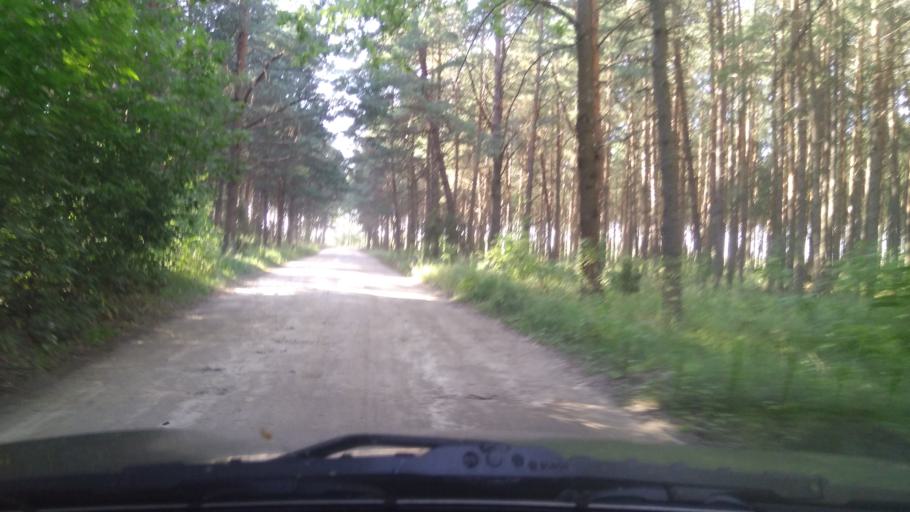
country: BY
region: Brest
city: Byelaazyorsk
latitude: 52.4449
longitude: 25.1712
